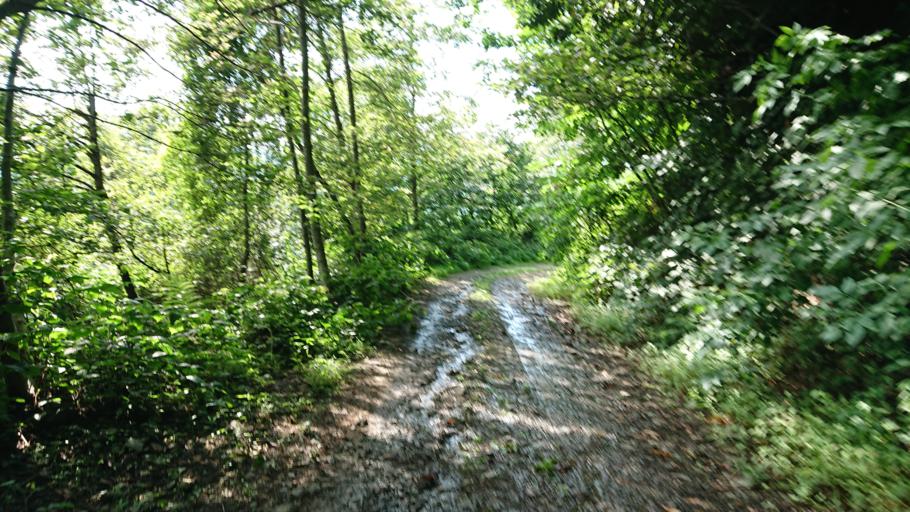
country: TR
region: Rize
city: Rize
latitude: 40.9780
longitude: 40.4987
